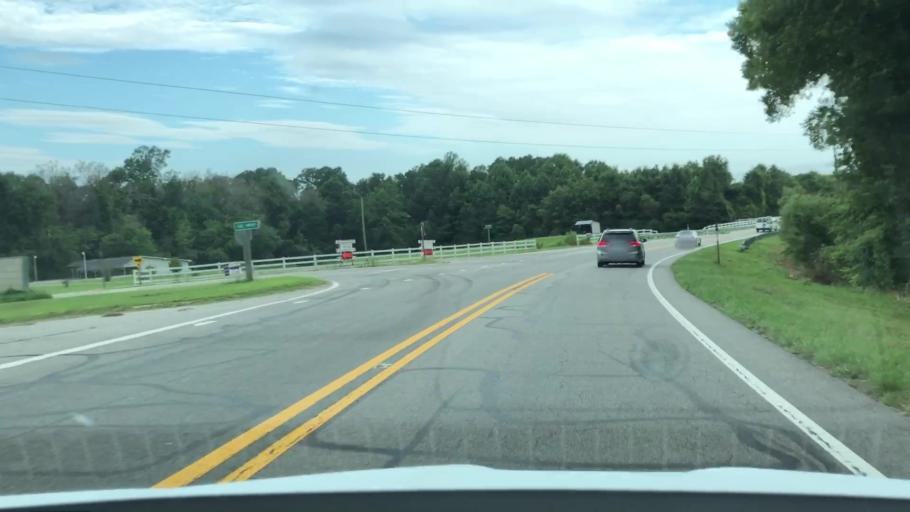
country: US
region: North Carolina
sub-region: Lenoir County
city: Kinston
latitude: 35.1572
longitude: -77.5530
